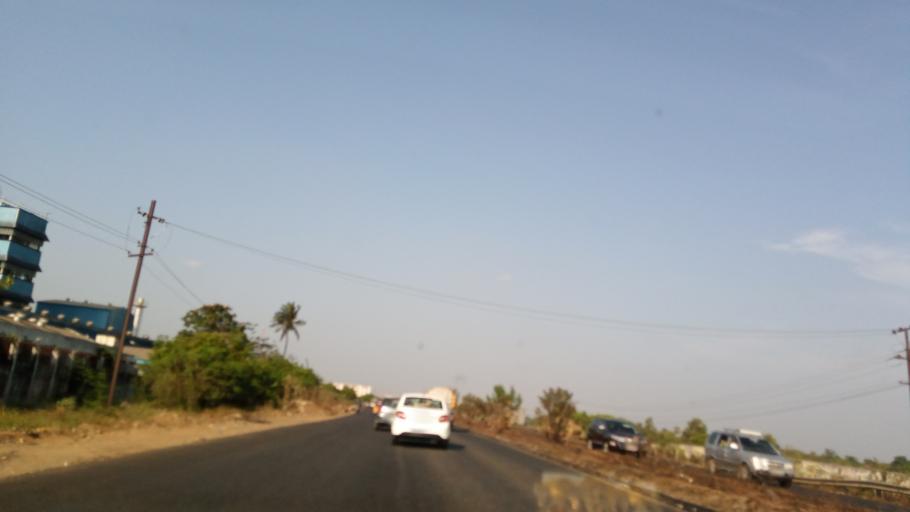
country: IN
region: Tamil Nadu
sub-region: Kancheepuram
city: Nandambakkam
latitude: 13.0171
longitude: 80.0080
